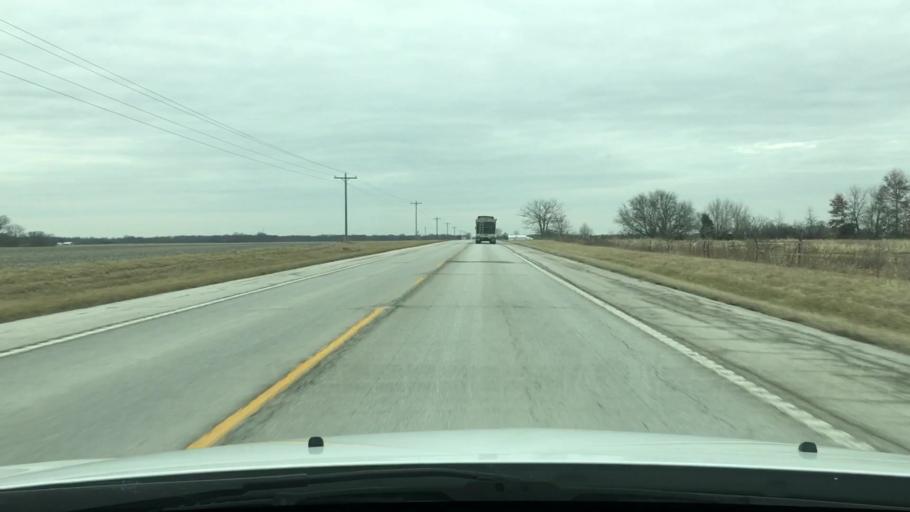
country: US
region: Missouri
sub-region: Montgomery County
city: Wellsville
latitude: 39.1798
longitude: -91.6473
